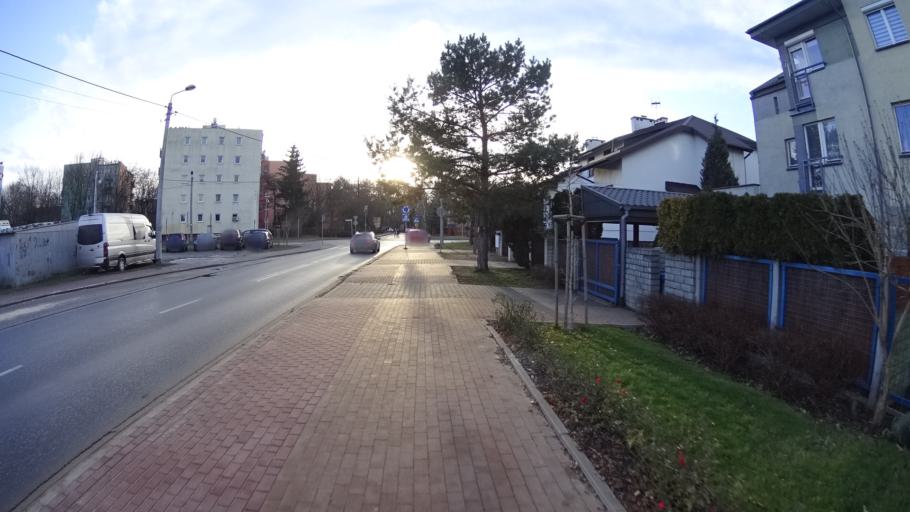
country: PL
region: Masovian Voivodeship
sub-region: Powiat warszawski zachodni
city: Ozarow Mazowiecki
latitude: 52.2133
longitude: 20.7990
